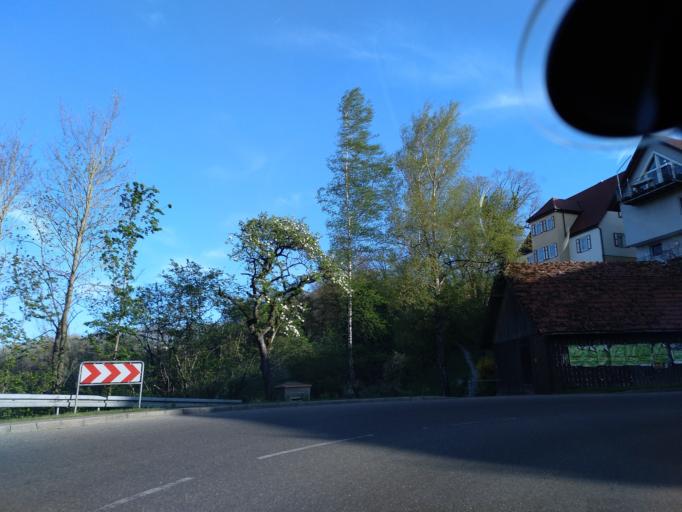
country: DE
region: Baden-Wuerttemberg
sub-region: Regierungsbezirk Stuttgart
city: Kirchberg an der Jagst
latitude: 49.2019
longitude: 9.9831
